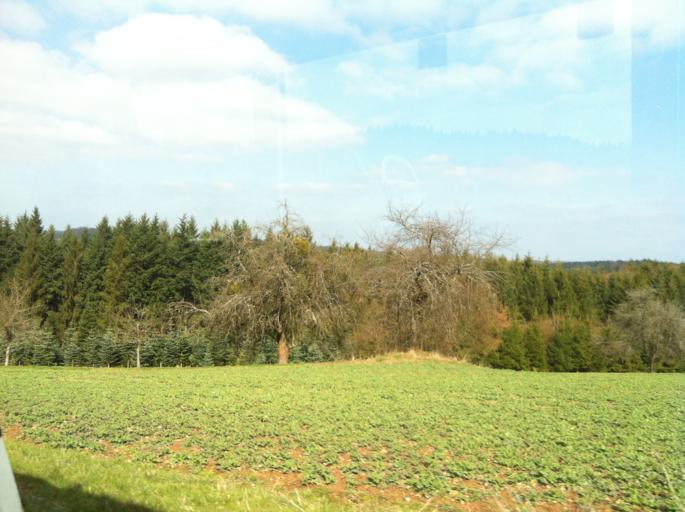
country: DE
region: Baden-Wuerttemberg
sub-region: Karlsruhe Region
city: Limbach
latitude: 49.4720
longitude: 9.2158
